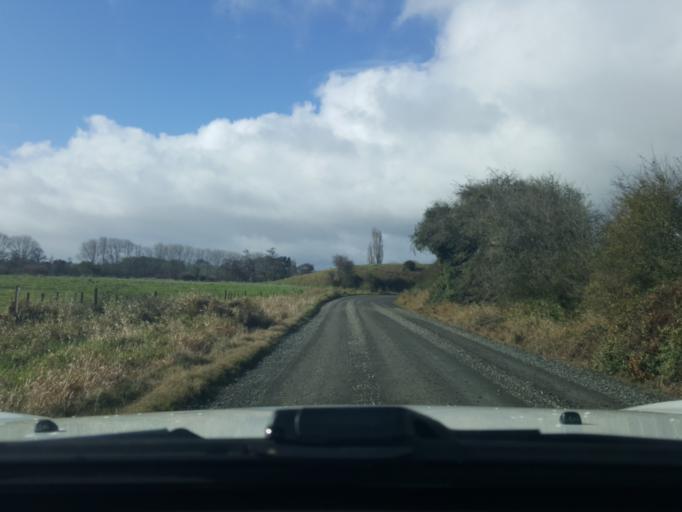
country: NZ
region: Waikato
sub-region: Waikato District
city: Te Kauwhata
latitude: -37.4213
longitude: 175.0723
